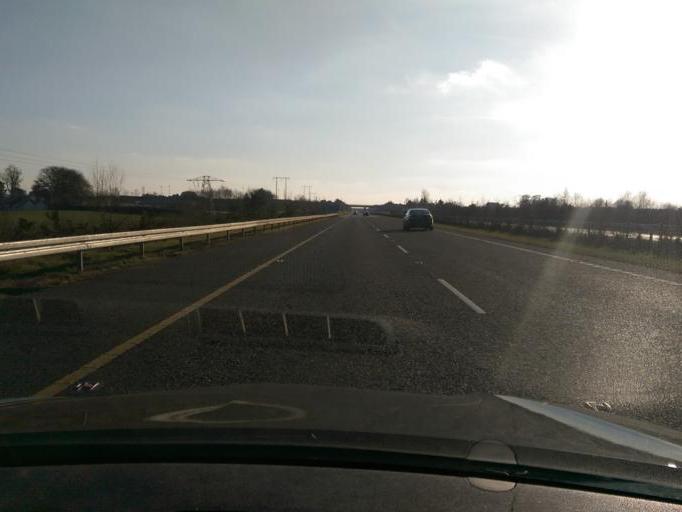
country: IE
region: Leinster
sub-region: Laois
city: Stradbally
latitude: 53.0713
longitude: -7.2100
